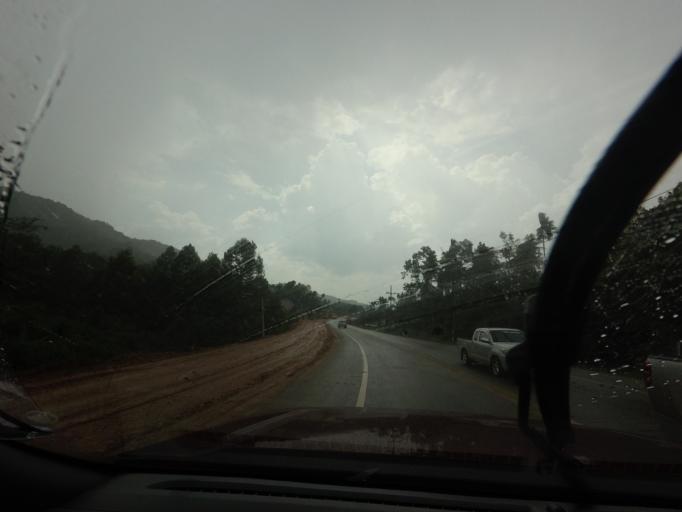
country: TH
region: Yala
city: Krong Pi Nang
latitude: 6.3811
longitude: 101.2961
